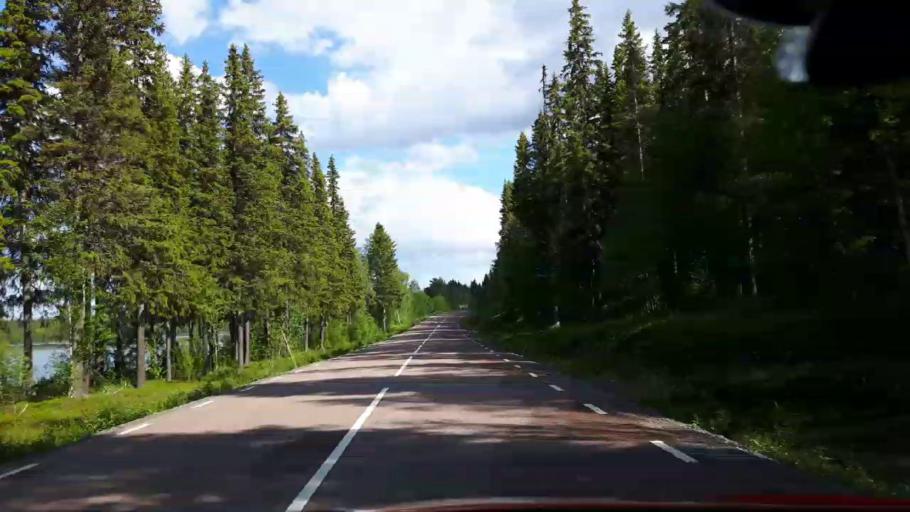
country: SE
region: Jaemtland
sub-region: Krokoms Kommun
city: Valla
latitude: 63.9574
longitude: 14.1935
